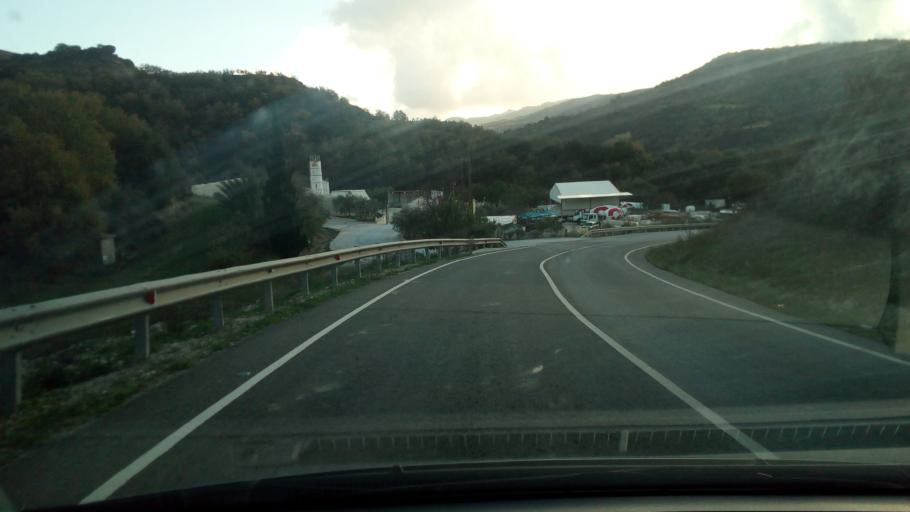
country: CY
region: Pafos
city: Polis
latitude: 34.9547
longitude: 32.4705
